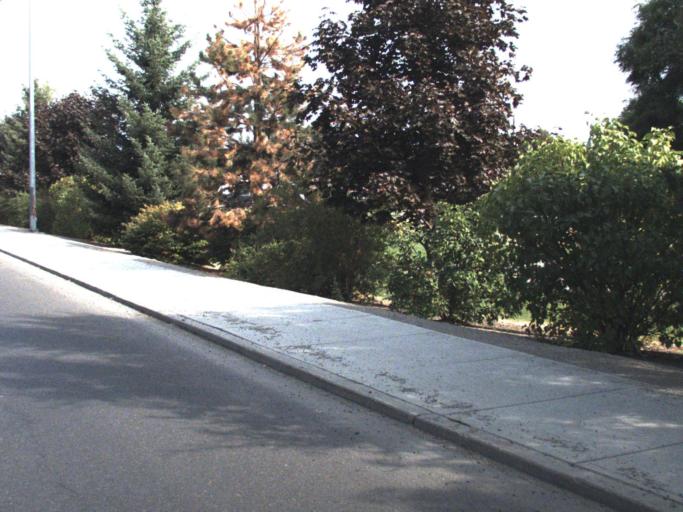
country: US
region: Washington
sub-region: Spokane County
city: Country Homes
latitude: 47.7468
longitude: -117.4114
